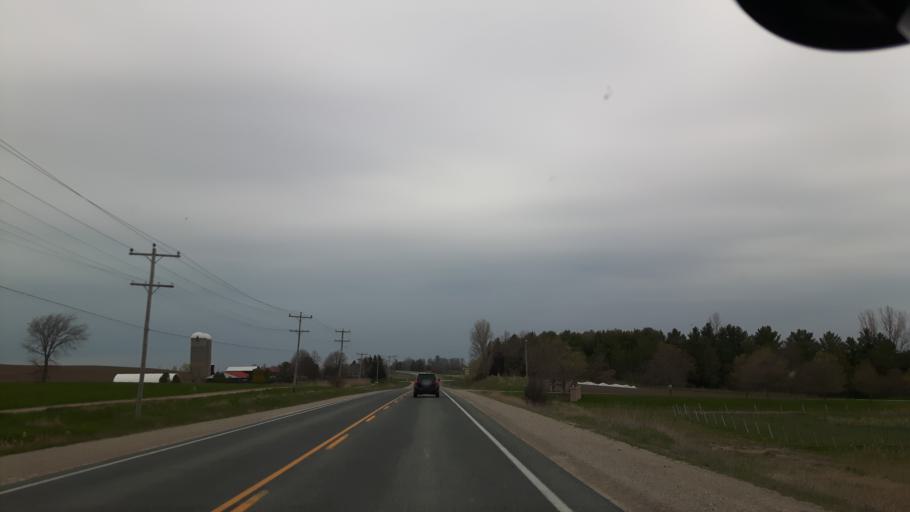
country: CA
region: Ontario
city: Goderich
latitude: 43.6844
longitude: -81.6302
